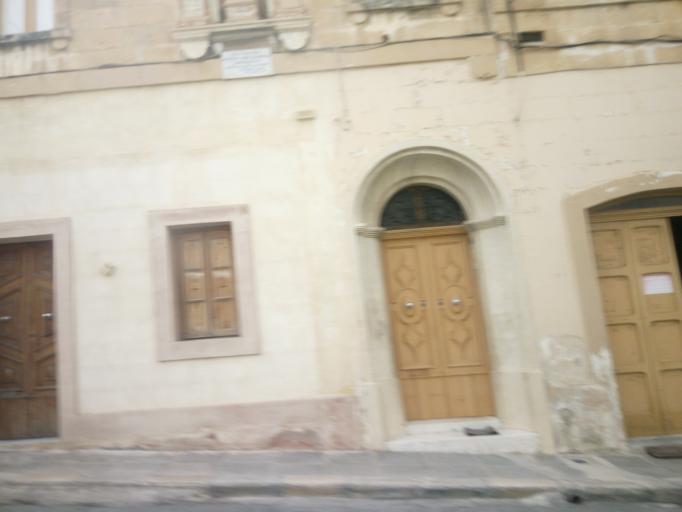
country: MT
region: Luqa
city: Luqa
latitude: 35.8626
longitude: 14.4891
